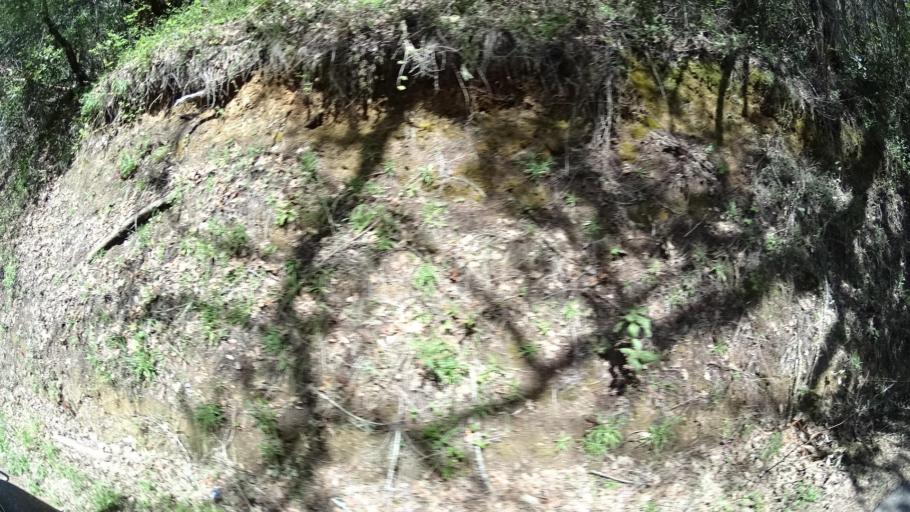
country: US
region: California
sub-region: Humboldt County
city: Redway
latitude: 40.2879
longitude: -123.6491
